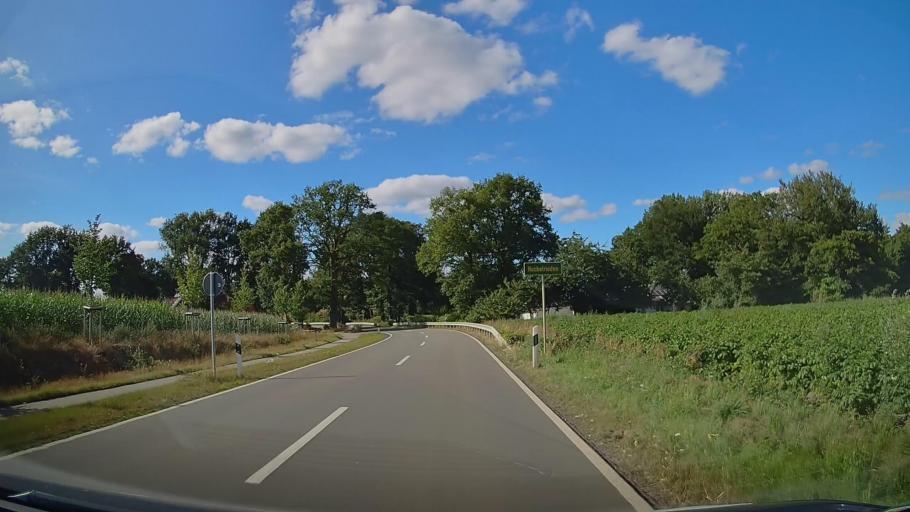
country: DE
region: Lower Saxony
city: Loningen
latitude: 52.7040
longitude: 7.7572
